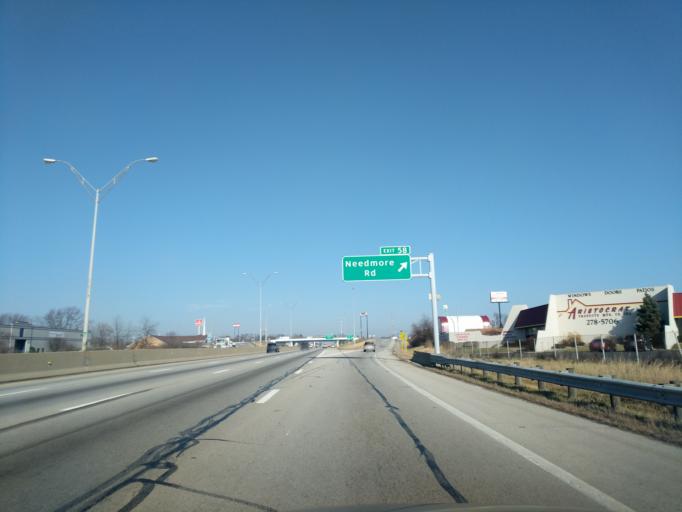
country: US
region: Ohio
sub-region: Montgomery County
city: Northridge
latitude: 39.8160
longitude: -84.1889
